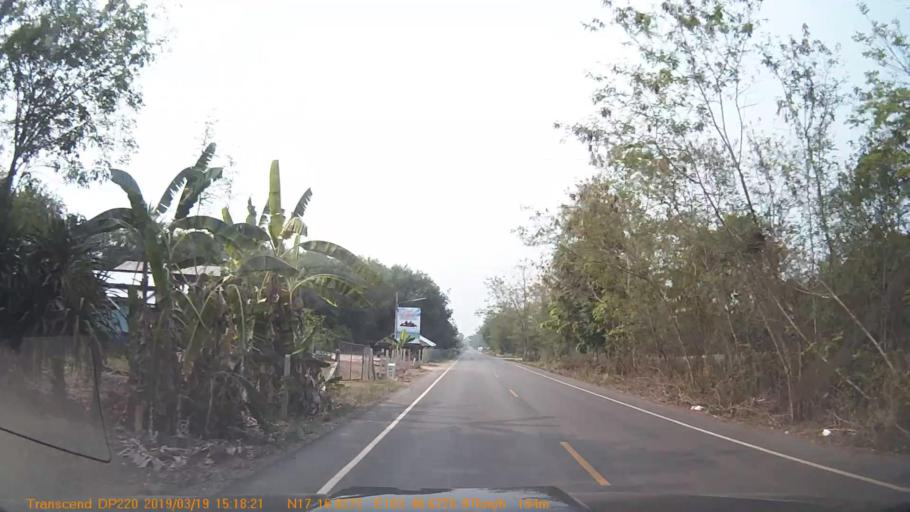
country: TH
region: Sakon Nakhon
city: Phanna Nikhom
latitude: 17.2824
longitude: 103.7777
